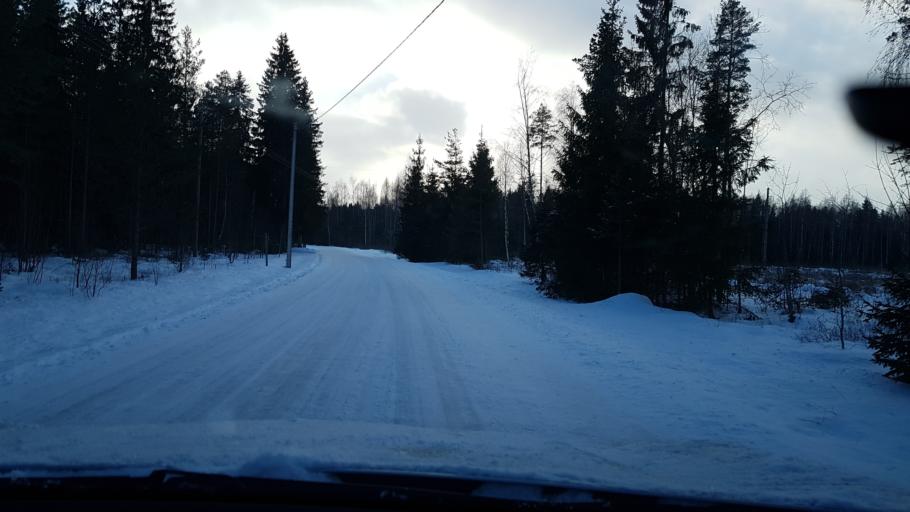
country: EE
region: Harju
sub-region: Nissi vald
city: Turba
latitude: 59.2142
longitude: 24.1413
